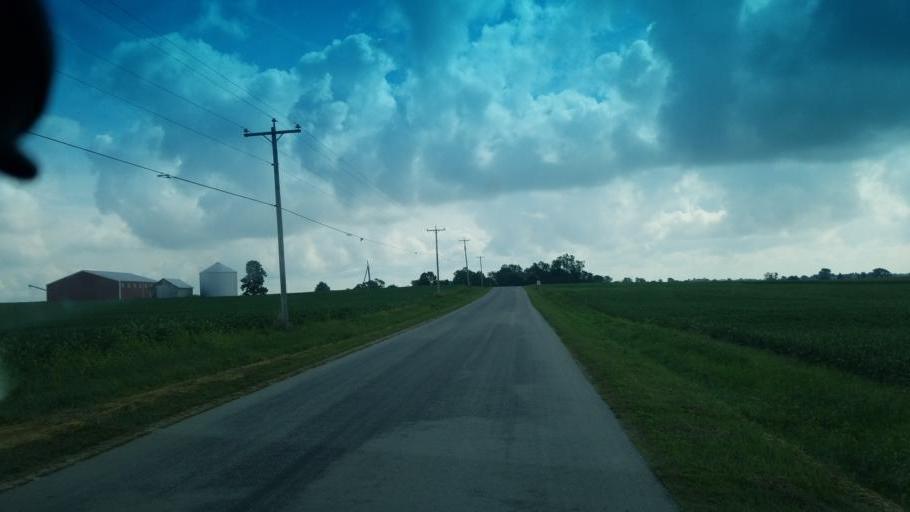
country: US
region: Ohio
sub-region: Hardin County
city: Forest
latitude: 40.8699
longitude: -83.4999
